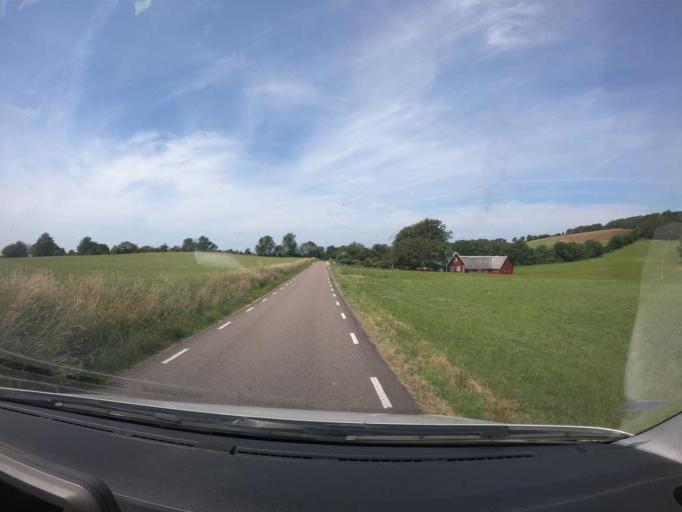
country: SE
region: Skane
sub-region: Bastads Kommun
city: Bastad
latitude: 56.4589
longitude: 12.7265
